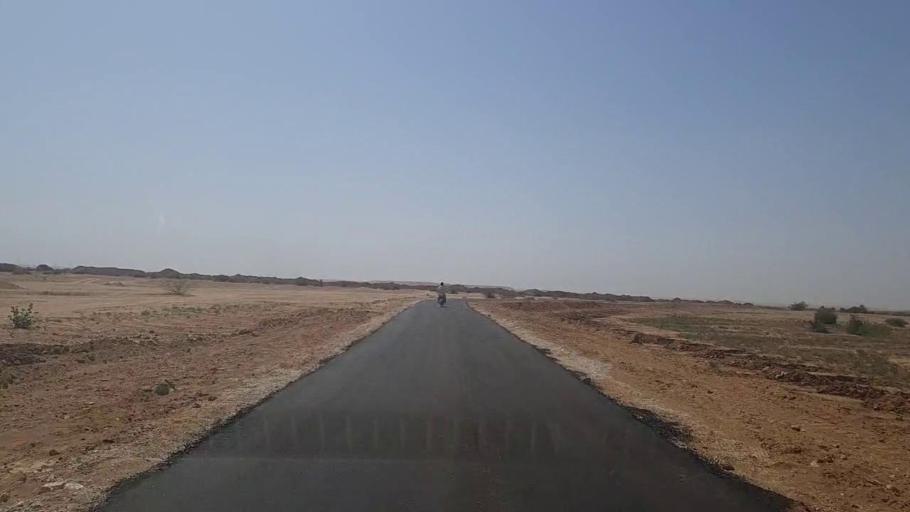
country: PK
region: Sindh
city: Kotri
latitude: 25.1463
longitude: 68.2005
